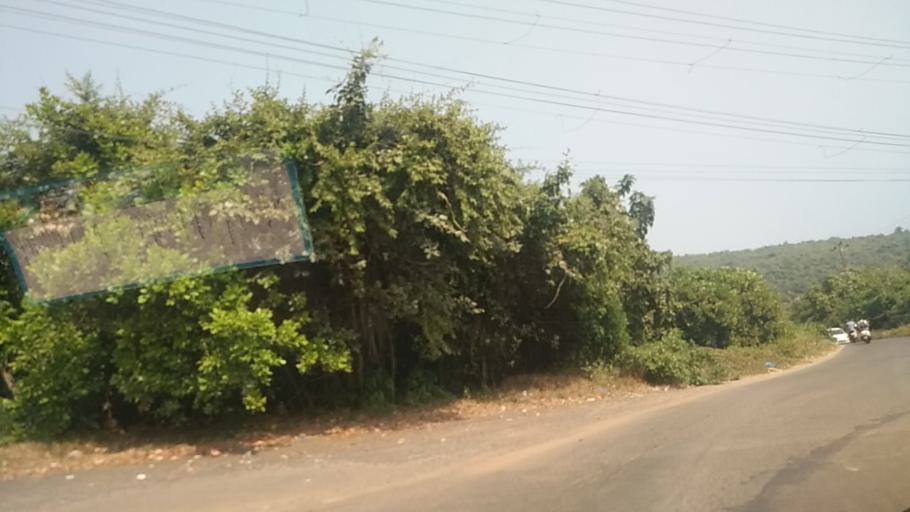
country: IN
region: Goa
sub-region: North Goa
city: Arambol
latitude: 15.6751
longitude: 73.7094
